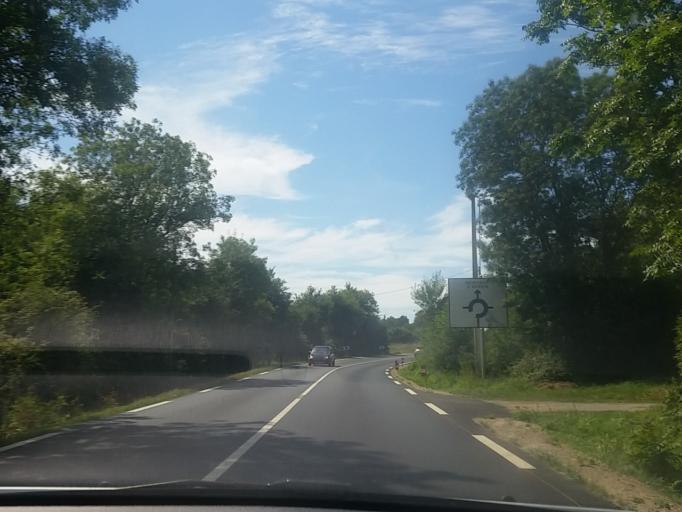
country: FR
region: Pays de la Loire
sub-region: Departement de la Loire-Atlantique
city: Vue
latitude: 47.1997
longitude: -1.8663
